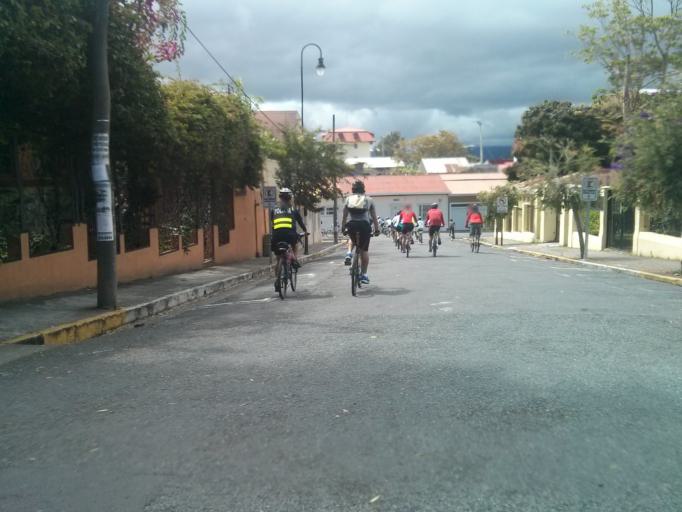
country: CR
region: San Jose
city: San Jose
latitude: 9.9372
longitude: -84.0725
